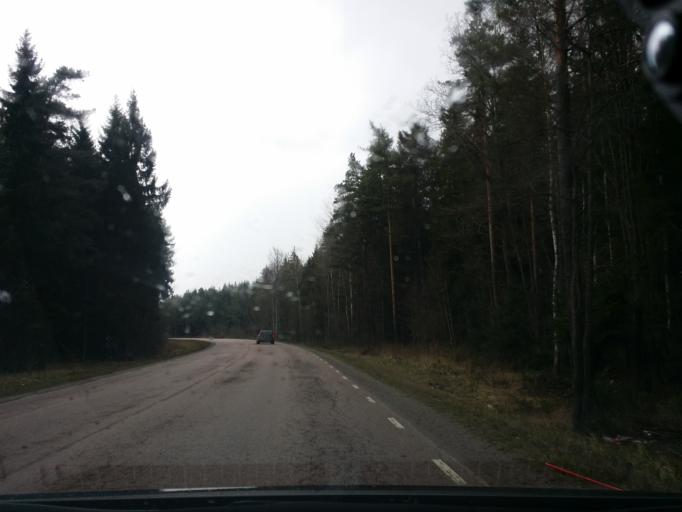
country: SE
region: Uppsala
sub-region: Enkopings Kommun
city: Enkoping
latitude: 59.6335
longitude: 17.1442
